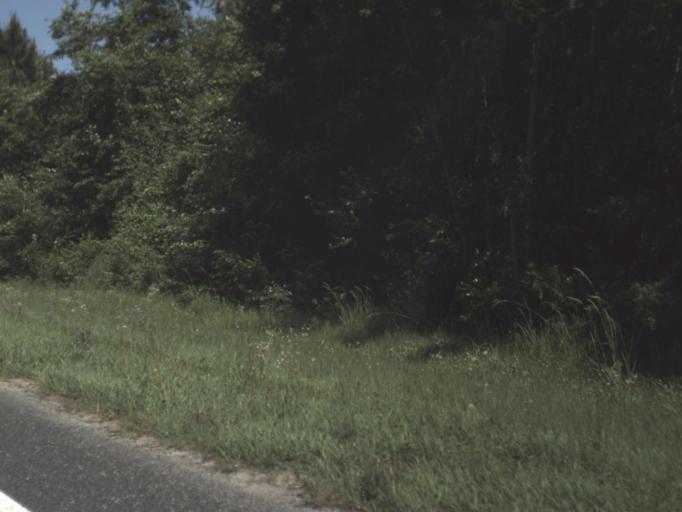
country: US
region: Florida
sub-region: Columbia County
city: Watertown
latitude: 30.2055
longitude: -82.4175
